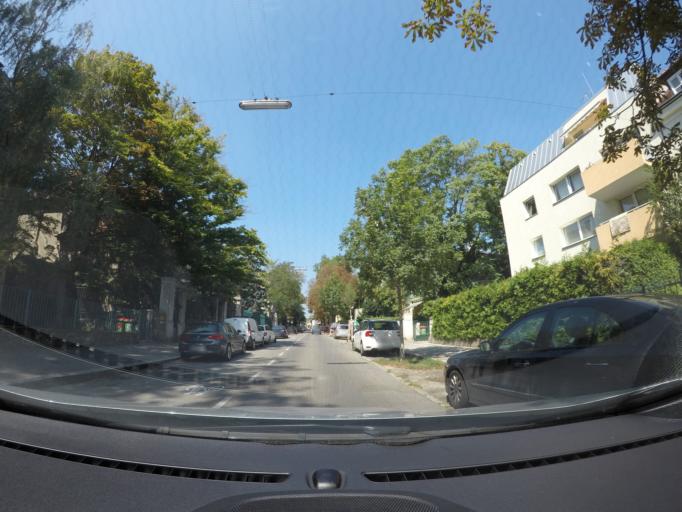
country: AT
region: Lower Austria
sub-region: Politischer Bezirk Modling
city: Perchtoldsdorf
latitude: 48.1883
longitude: 16.2908
